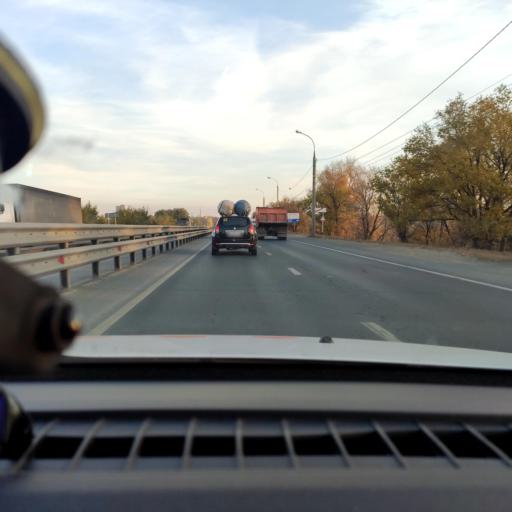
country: RU
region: Samara
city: Samara
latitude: 53.1214
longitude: 50.1685
